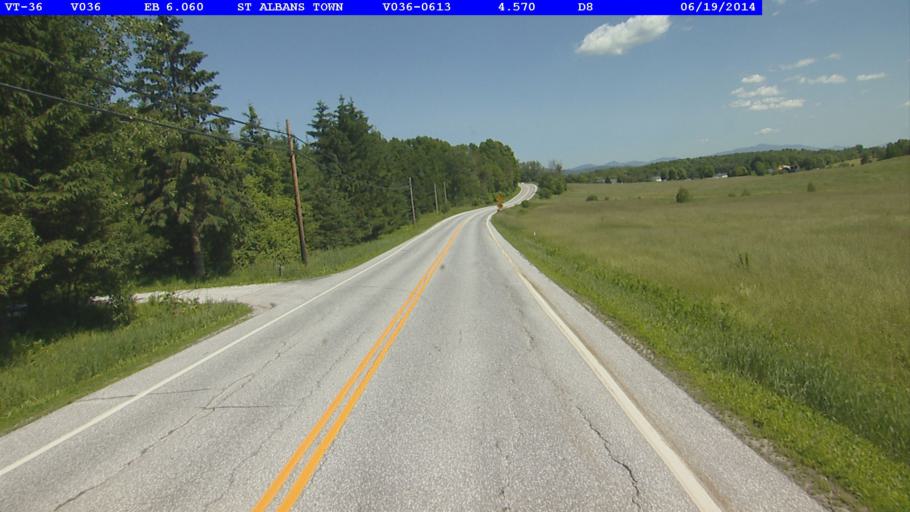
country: US
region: Vermont
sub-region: Franklin County
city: Saint Albans
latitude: 44.7924
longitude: -73.0441
